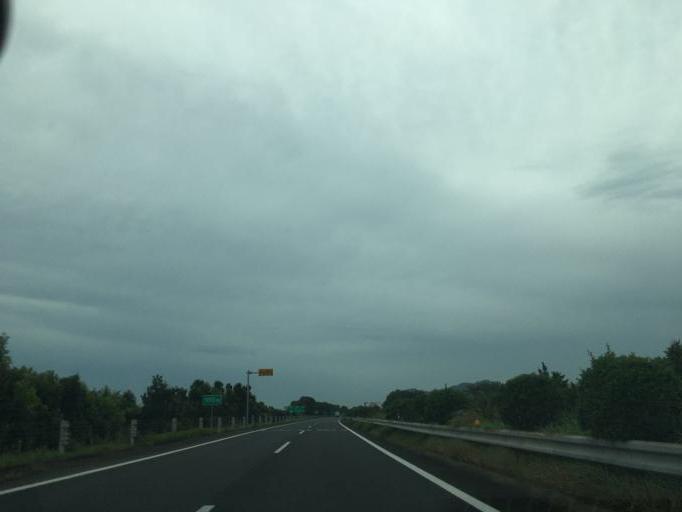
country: JP
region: Saga Prefecture
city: Saga-shi
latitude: 33.3084
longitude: 130.2429
